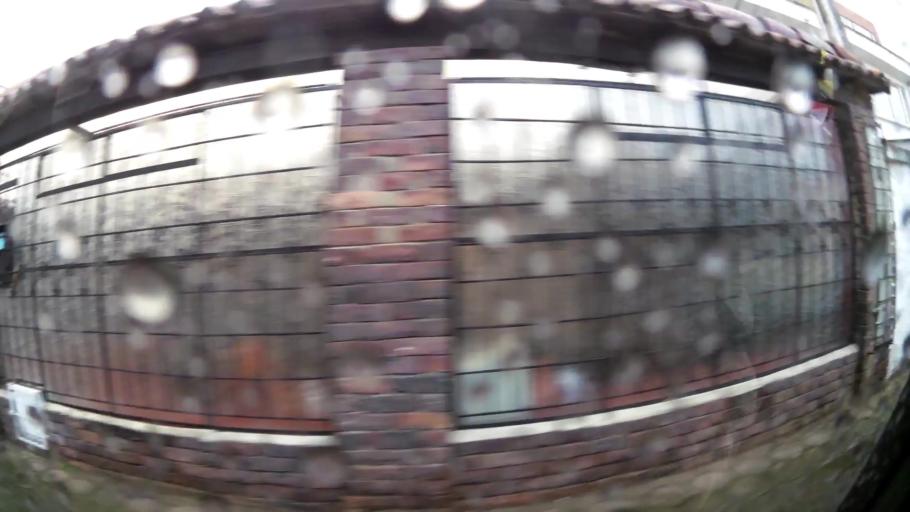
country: CO
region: Cundinamarca
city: Chia
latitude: 4.8575
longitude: -74.0560
